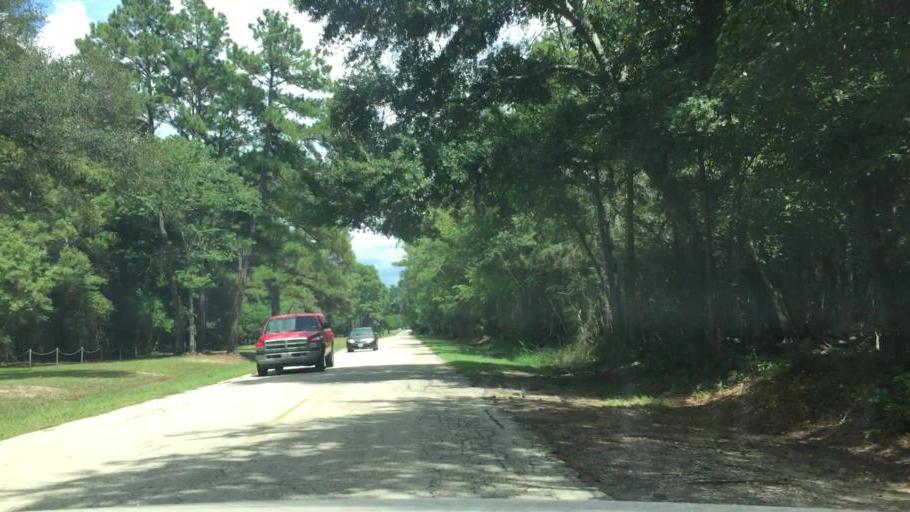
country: US
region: Texas
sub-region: Harris County
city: Jersey Village
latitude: 29.8133
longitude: -95.6253
